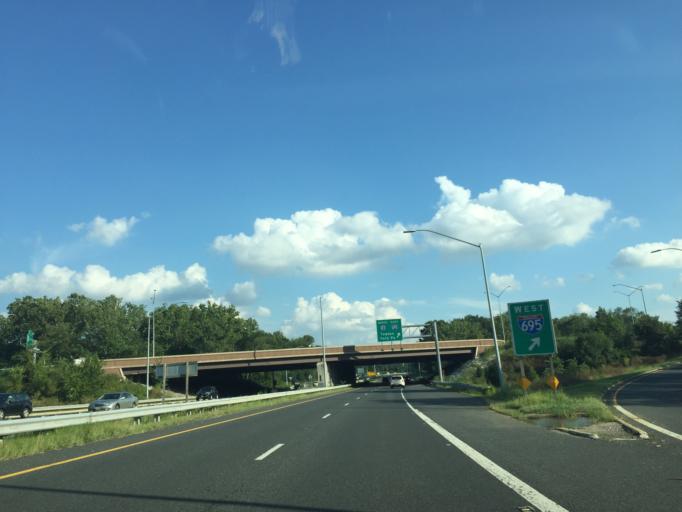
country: US
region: Maryland
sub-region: Baltimore County
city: Mays Chapel
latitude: 39.4127
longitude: -76.6645
